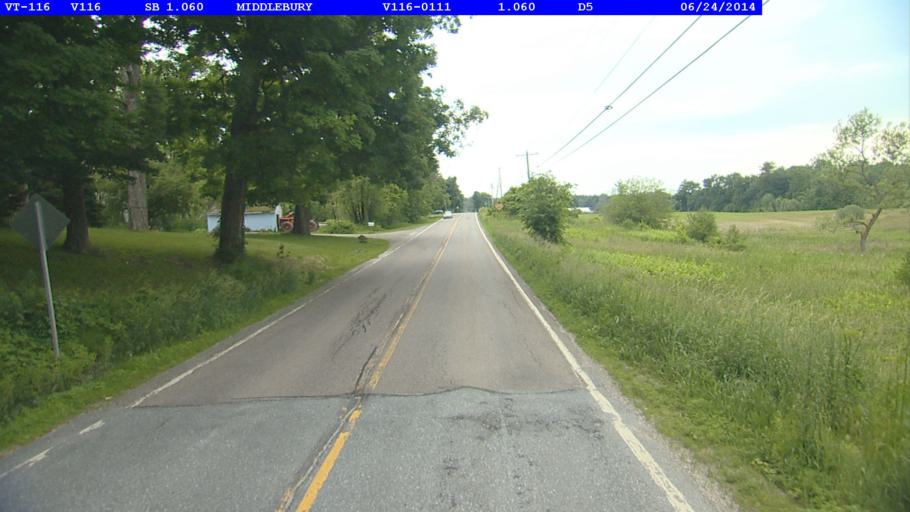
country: US
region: Vermont
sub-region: Addison County
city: Middlebury (village)
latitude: 43.9802
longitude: -73.1057
